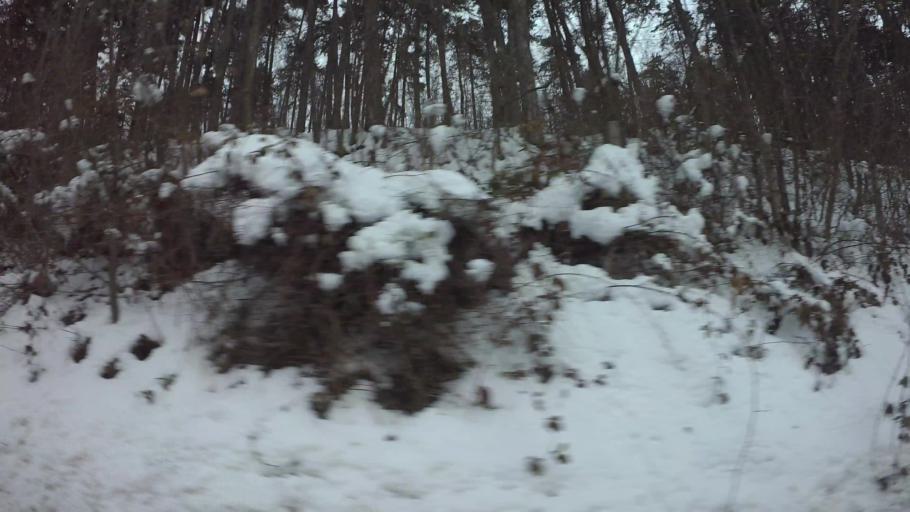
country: BA
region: Federation of Bosnia and Herzegovina
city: Kobilja Glava
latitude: 43.8650
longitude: 18.4437
